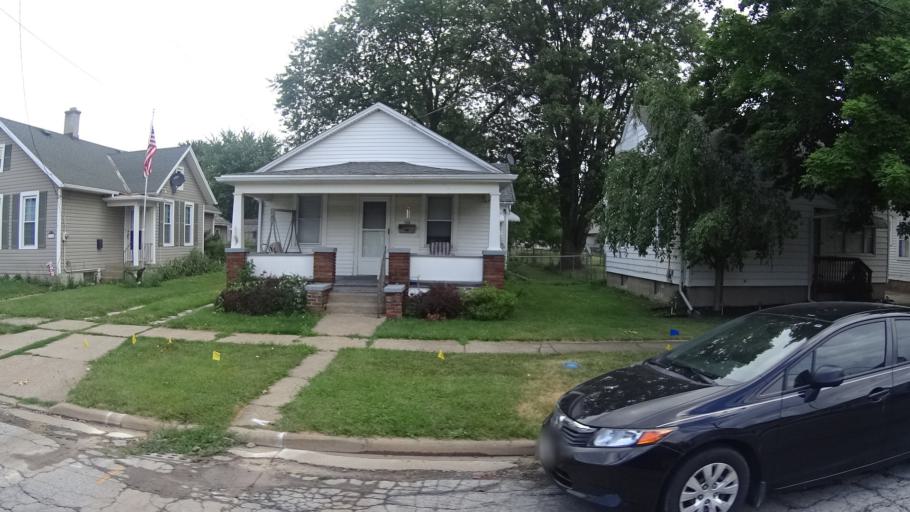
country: US
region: Ohio
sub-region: Erie County
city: Sandusky
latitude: 41.4446
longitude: -82.7276
